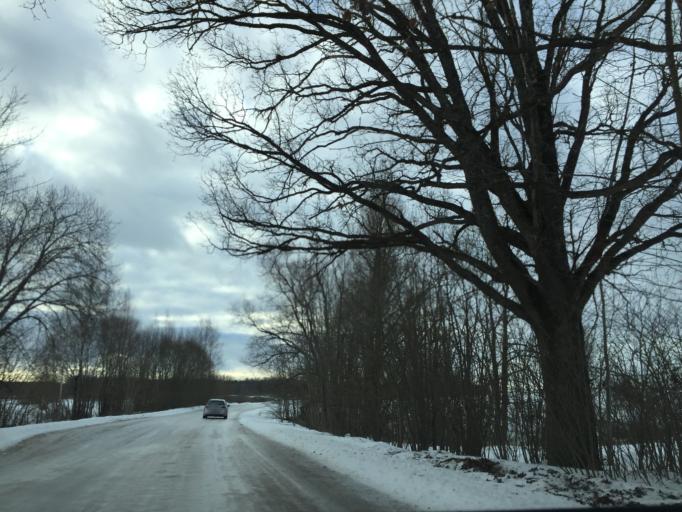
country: LV
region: Lielvarde
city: Lielvarde
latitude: 56.6098
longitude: 24.7622
